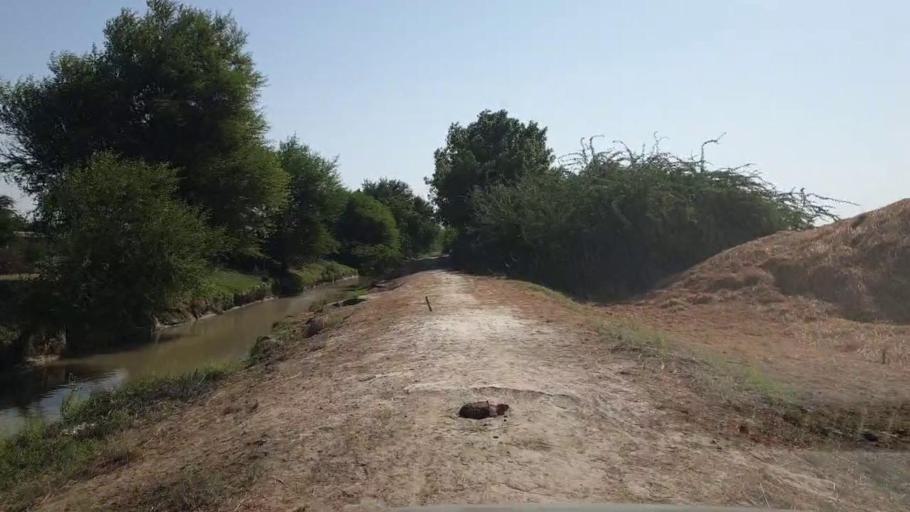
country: PK
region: Sindh
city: Kadhan
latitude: 24.6290
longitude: 68.9936
